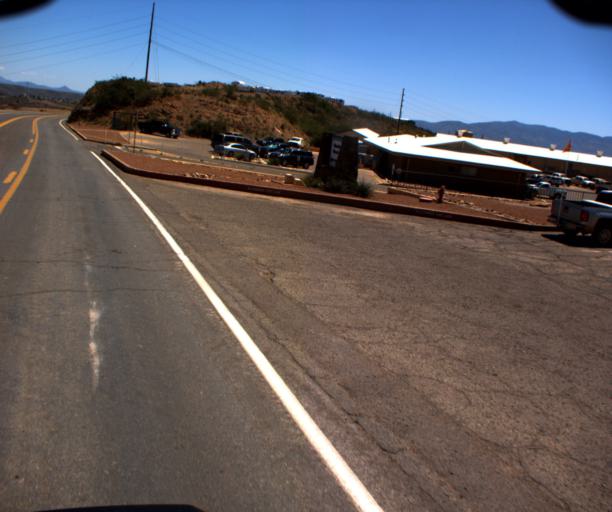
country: US
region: Arizona
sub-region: Greenlee County
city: Morenci
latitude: 33.0636
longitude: -109.3351
